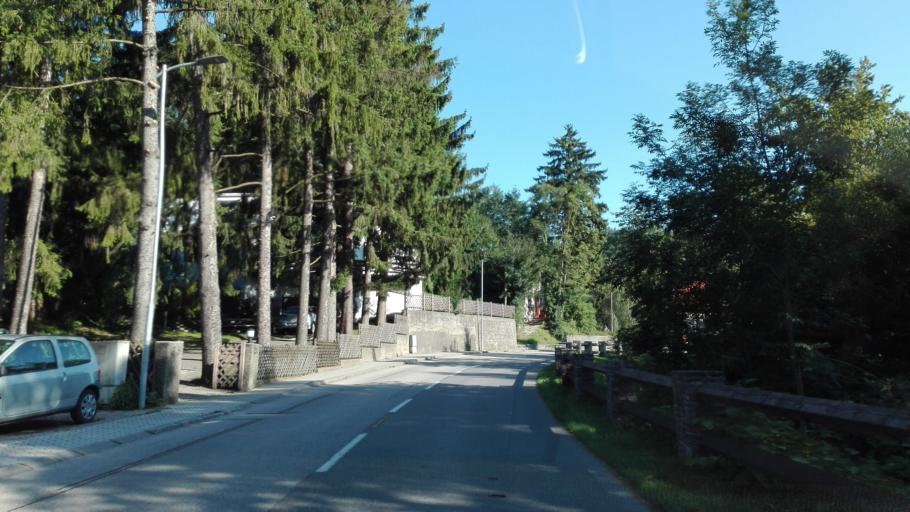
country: AT
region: Lower Austria
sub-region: Politischer Bezirk Sankt Polten
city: Altlengbach
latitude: 48.1116
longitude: 15.8829
